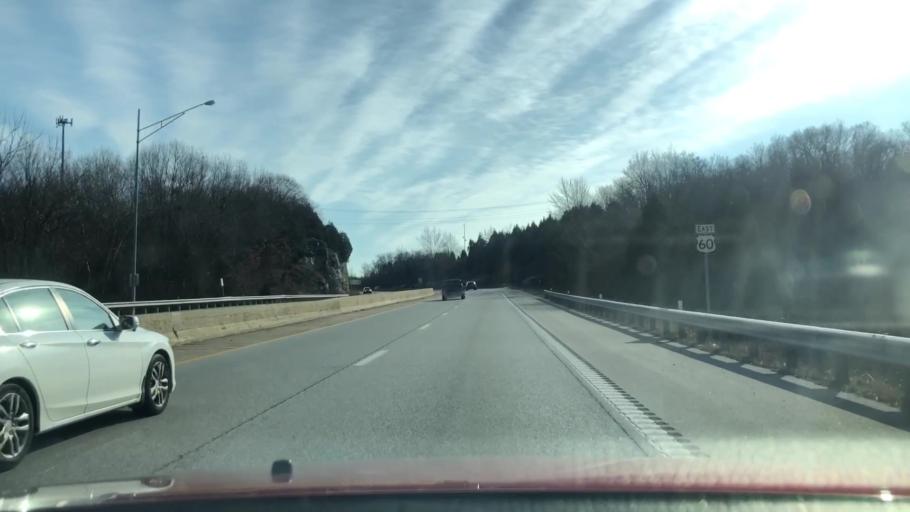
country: US
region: Missouri
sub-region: Christian County
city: Ozark
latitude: 37.1229
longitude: -93.2240
